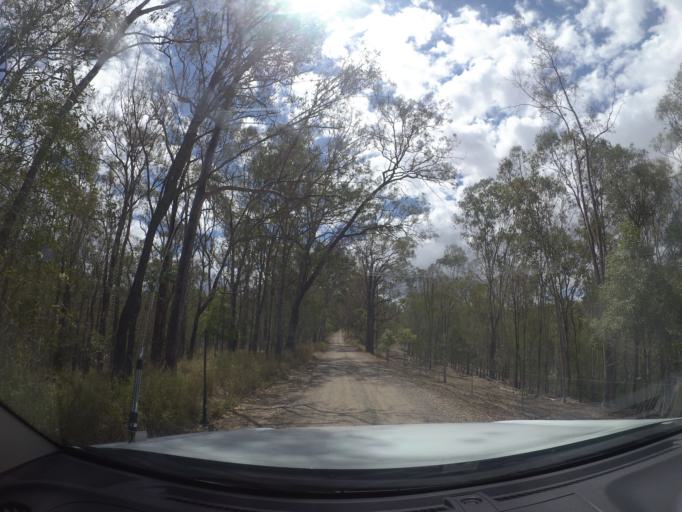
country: AU
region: Queensland
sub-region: Logan
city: Cedar Vale
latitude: -27.8998
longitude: 153.0454
